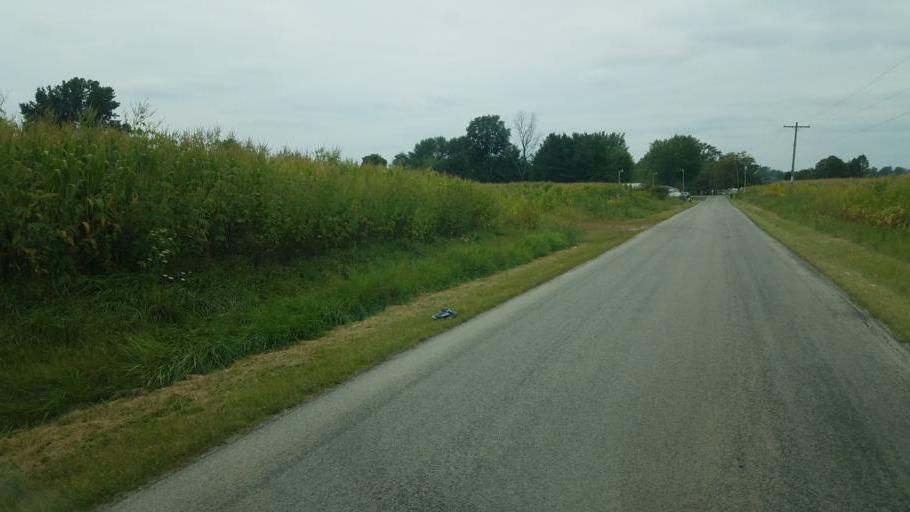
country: US
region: Ohio
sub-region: Morrow County
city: Mount Gilead
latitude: 40.5285
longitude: -82.8149
